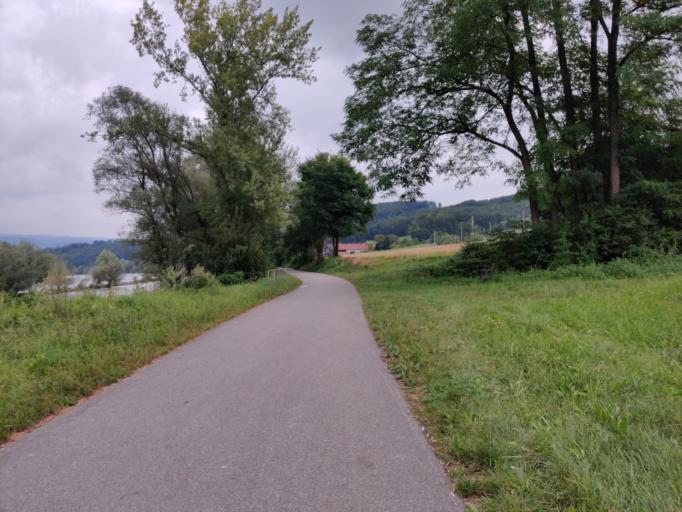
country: AT
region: Lower Austria
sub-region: Politischer Bezirk Melk
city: Ybbs an der Donau
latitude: 48.1753
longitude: 15.1196
